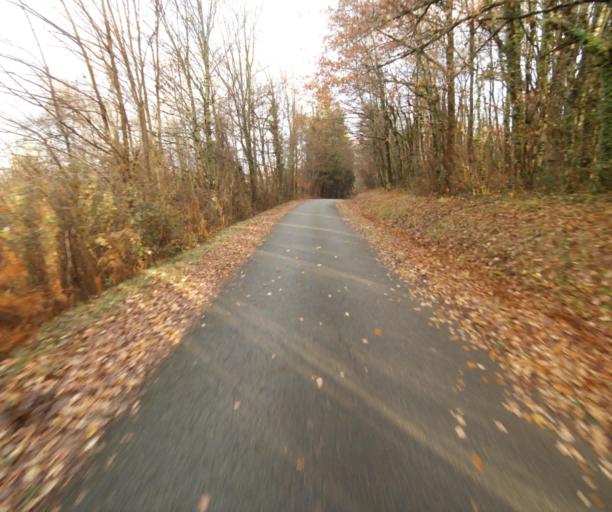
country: FR
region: Limousin
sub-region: Departement de la Correze
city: Saint-Mexant
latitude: 45.2611
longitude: 1.6278
